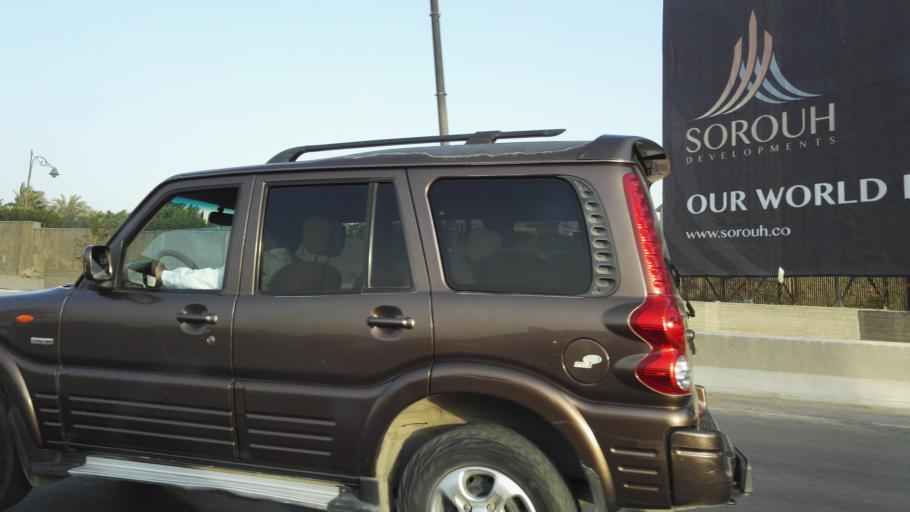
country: EG
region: Muhafazat al Qahirah
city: Cairo
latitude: 29.9973
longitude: 31.3931
